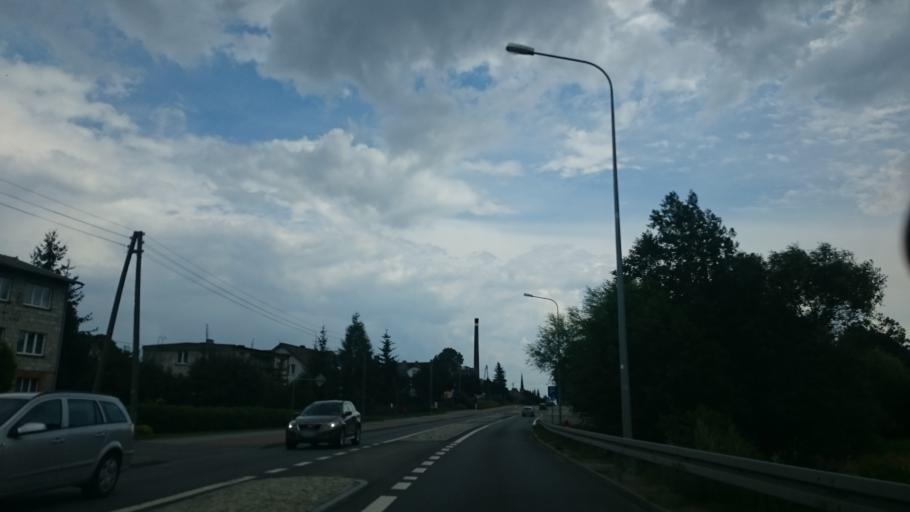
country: PL
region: Kujawsko-Pomorskie
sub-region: Powiat tucholski
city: Kesowo
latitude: 53.6491
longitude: 17.7031
